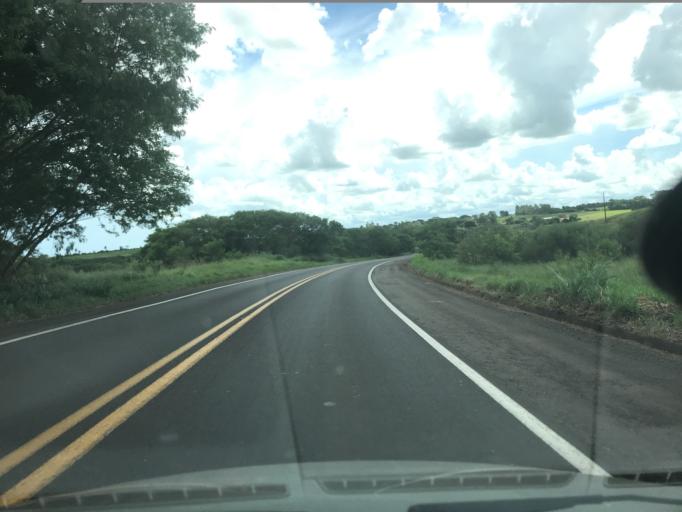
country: BR
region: Parana
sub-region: Cruzeiro Do Oeste
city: Cruzeiro do Oeste
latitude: -23.7886
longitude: -53.0288
